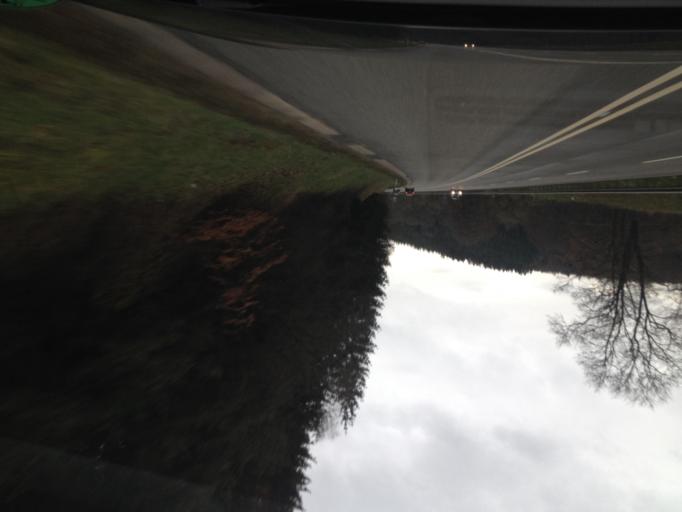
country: DE
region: Rheinland-Pfalz
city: Ellweiler
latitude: 49.6319
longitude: 7.1611
